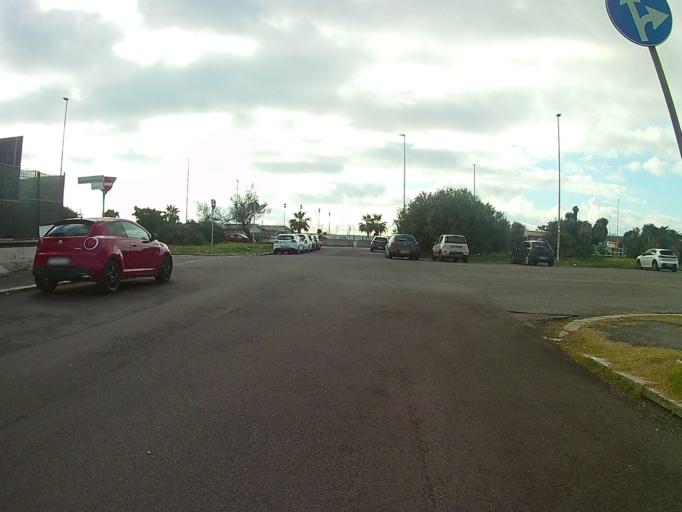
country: IT
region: Latium
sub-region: Citta metropolitana di Roma Capitale
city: Lido di Ostia
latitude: 41.7169
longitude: 12.3141
